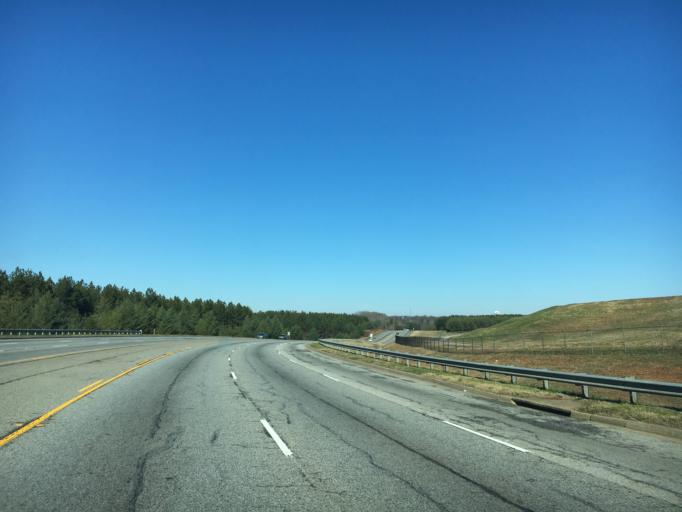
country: US
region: South Carolina
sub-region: Greenville County
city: Greer
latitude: 34.8794
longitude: -82.2314
